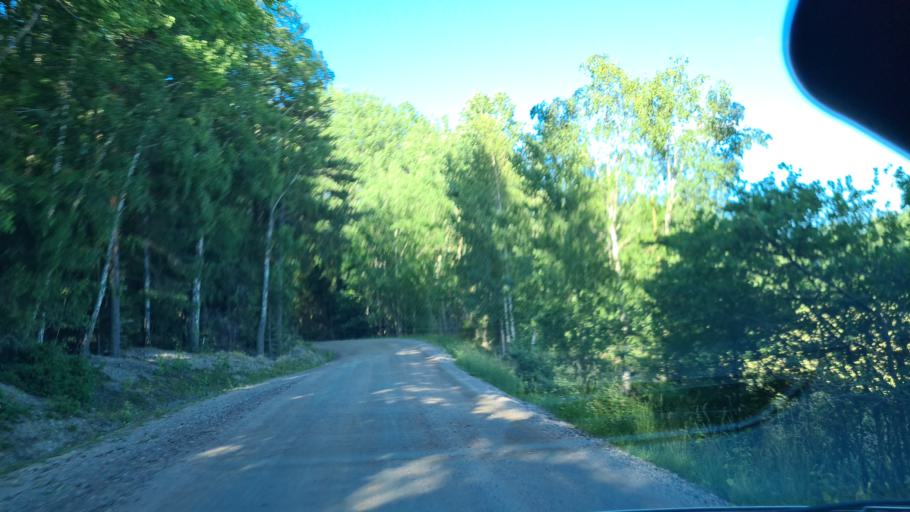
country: SE
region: Soedermanland
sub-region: Nykopings Kommun
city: Nykoping
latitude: 58.9202
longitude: 17.0256
